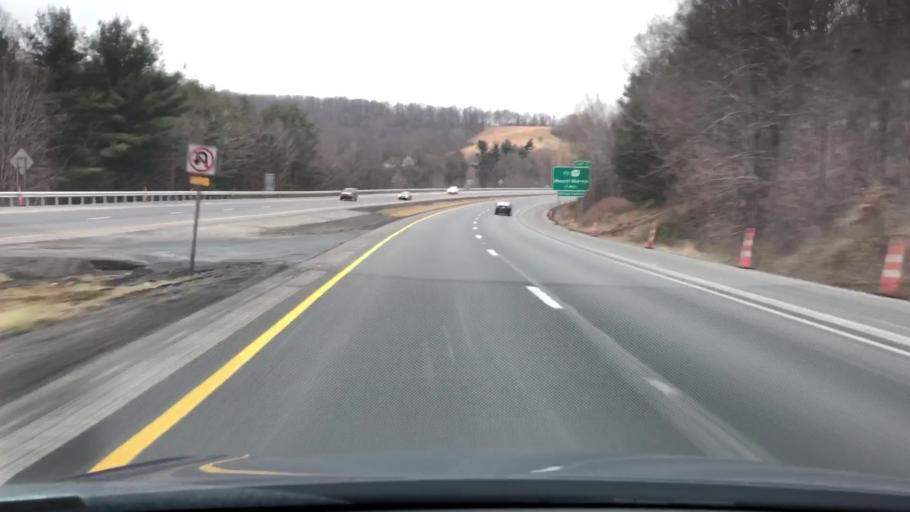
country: US
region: West Virginia
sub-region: Monongalia County
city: Star City
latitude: 39.7162
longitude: -80.0602
